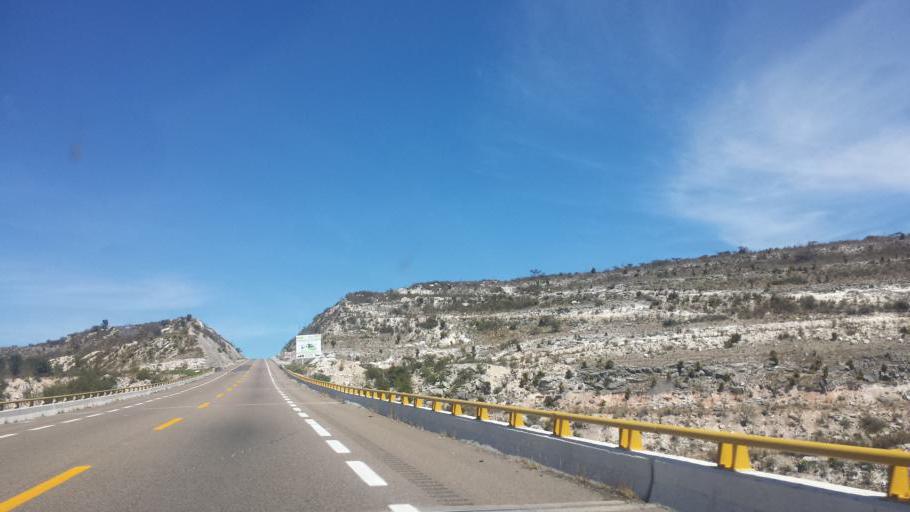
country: MX
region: Oaxaca
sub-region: Villa Tejupam de la Union
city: Villa Tejupam de la Union
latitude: 17.9094
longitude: -97.3642
